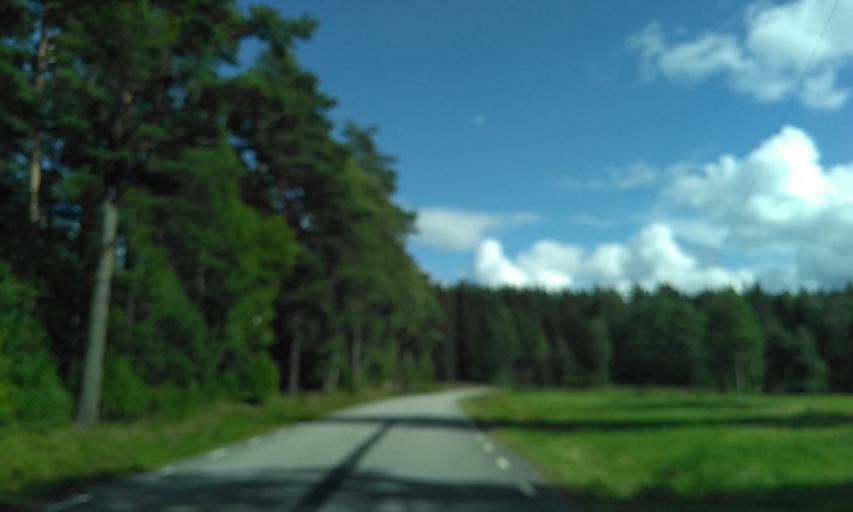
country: SE
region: Vaestra Goetaland
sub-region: Vargarda Kommun
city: Vargarda
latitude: 57.9441
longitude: 12.7990
